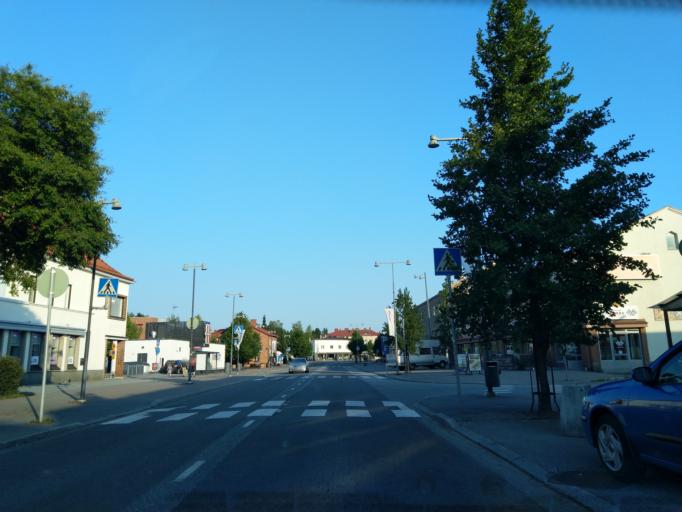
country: FI
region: Satakunta
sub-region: Pohjois-Satakunta
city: Kankaanpaeae
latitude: 61.8046
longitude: 22.3929
